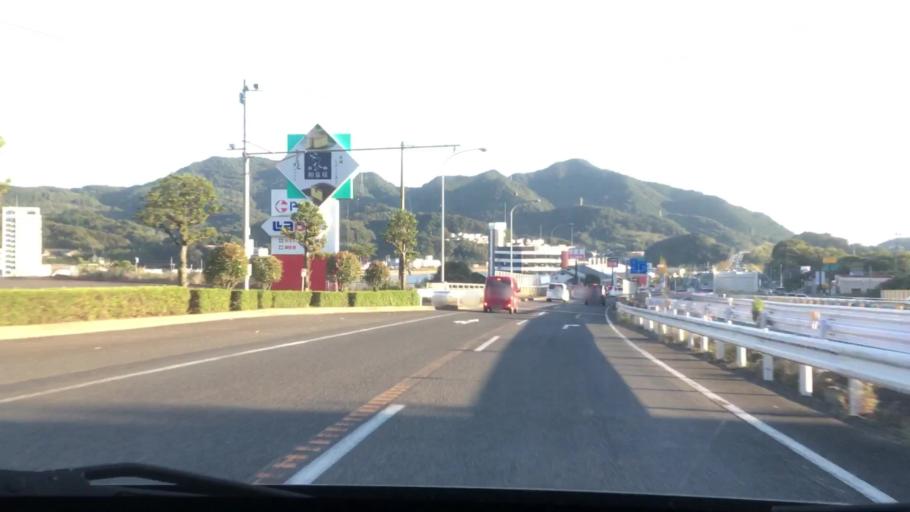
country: JP
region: Nagasaki
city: Sasebo
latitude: 33.1203
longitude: 129.7924
